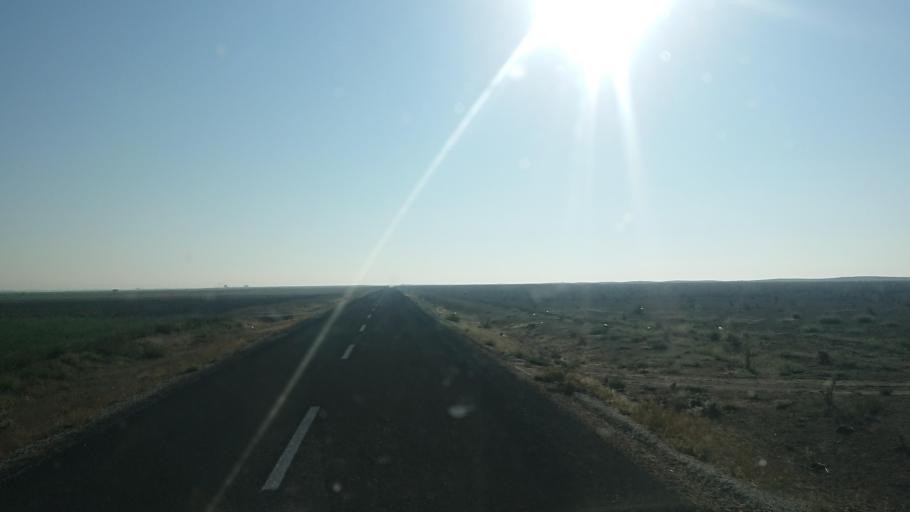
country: TR
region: Aksaray
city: Yesilova
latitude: 38.3878
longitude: 33.7672
